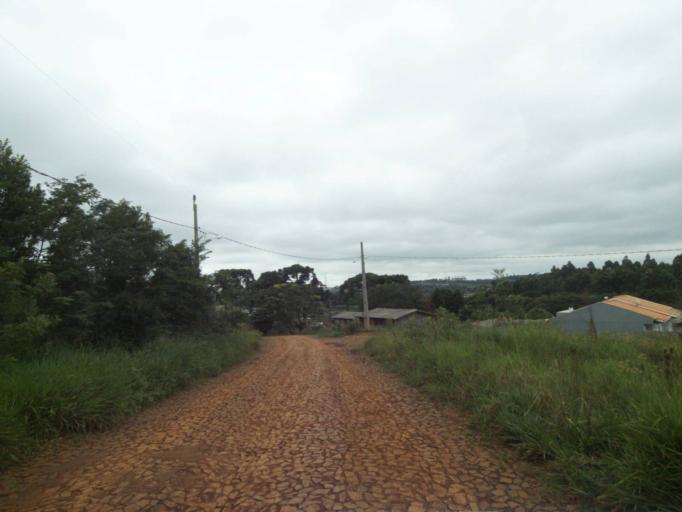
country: BR
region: Parana
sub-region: Pitanga
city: Pitanga
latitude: -24.9260
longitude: -51.8721
